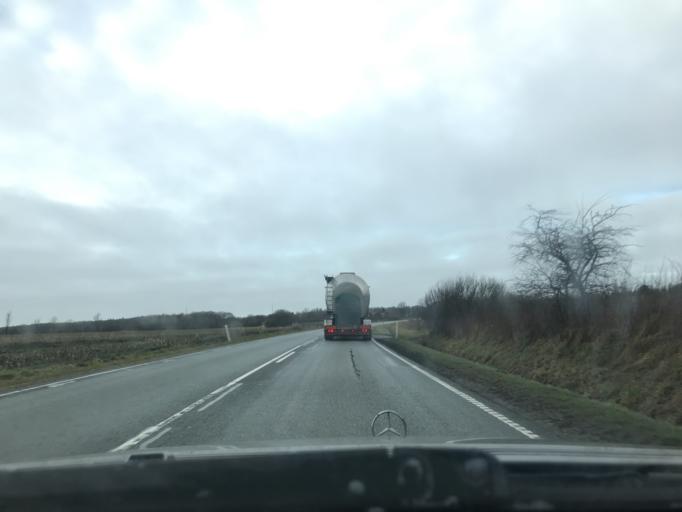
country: DK
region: South Denmark
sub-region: Haderslev Kommune
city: Gram
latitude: 55.2551
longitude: 8.9039
